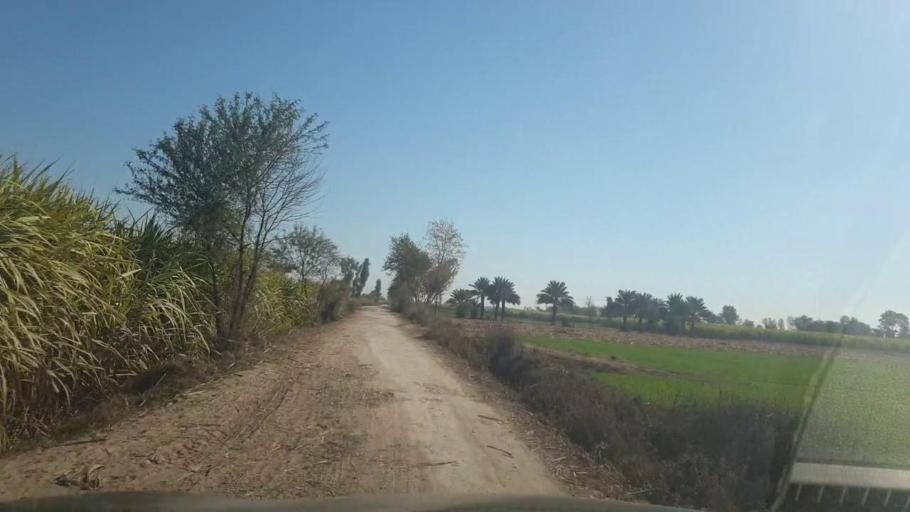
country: PK
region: Sindh
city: Ghotki
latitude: 27.9744
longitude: 69.3355
